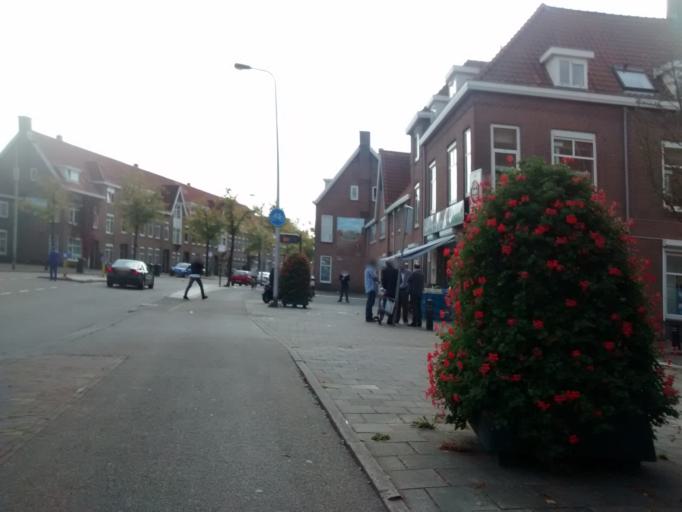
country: NL
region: Utrecht
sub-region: Gemeente Utrecht
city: Utrecht
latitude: 52.0717
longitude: 5.1137
